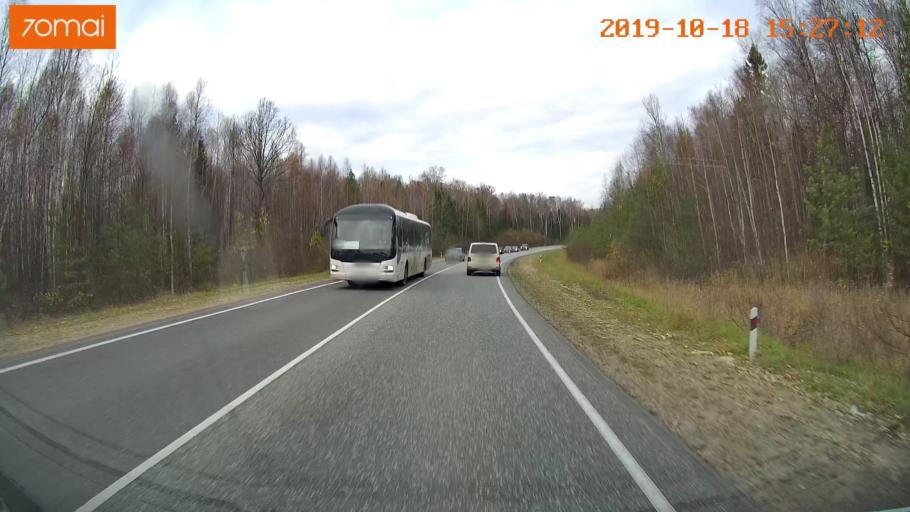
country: RU
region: Vladimir
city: Anopino
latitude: 55.7502
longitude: 40.6719
